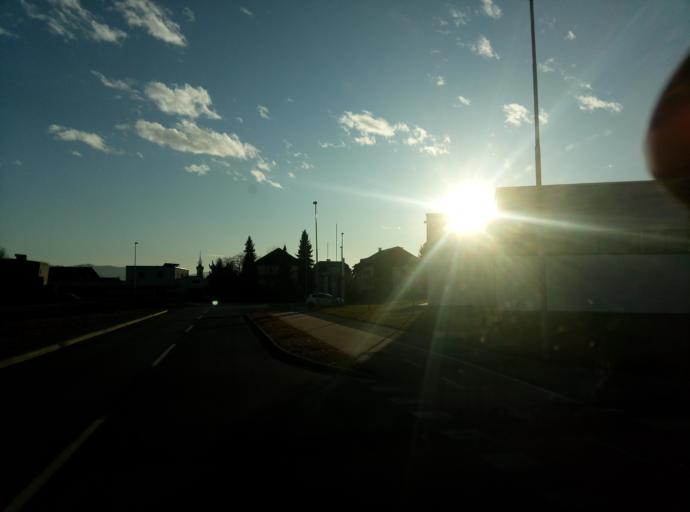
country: SI
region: Kranj
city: Kranj
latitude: 46.2303
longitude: 14.3696
